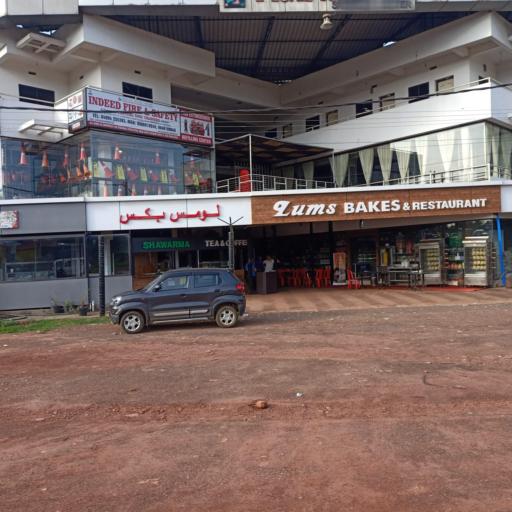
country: IN
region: Kerala
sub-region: Kasaragod District
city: Kasaragod
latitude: 12.5168
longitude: 75.0203
